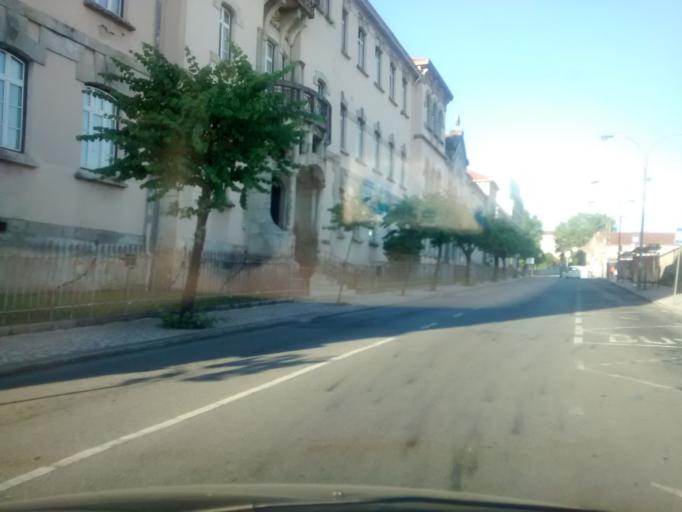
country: PT
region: Braga
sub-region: Braga
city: Braga
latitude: 41.5528
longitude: -8.4277
